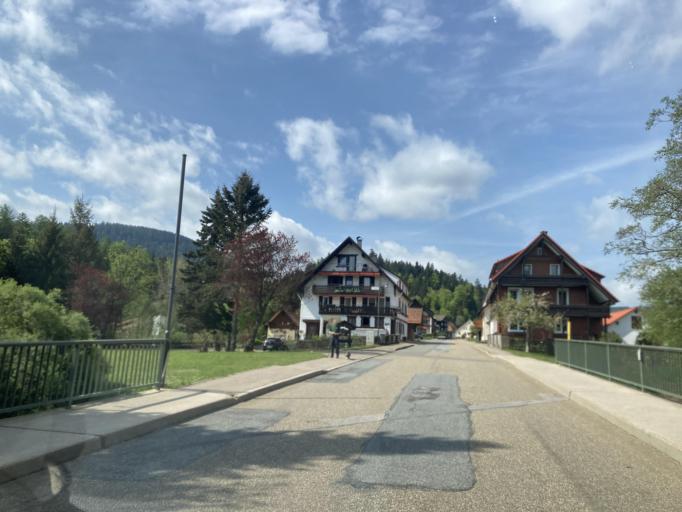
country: DE
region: Baden-Wuerttemberg
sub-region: Karlsruhe Region
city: Biberach
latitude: 48.5292
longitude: 8.2778
